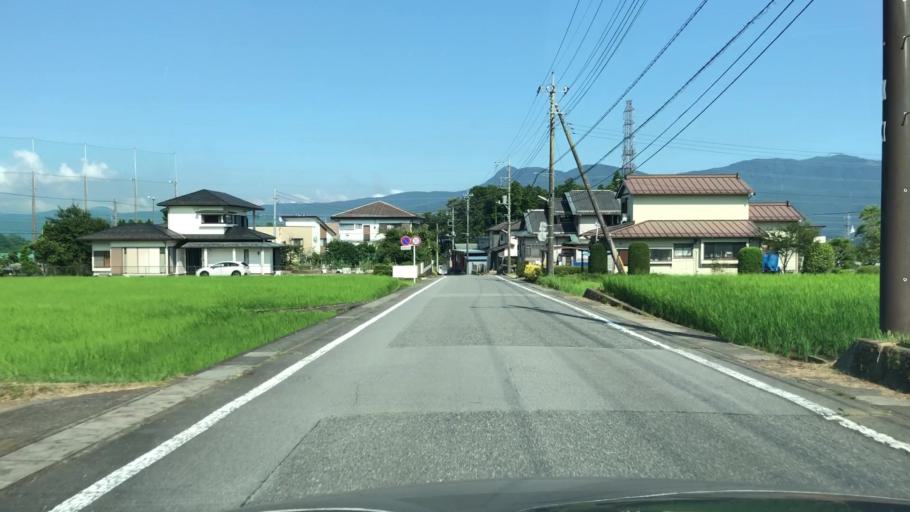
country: JP
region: Shizuoka
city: Gotemba
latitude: 35.3122
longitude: 138.9130
